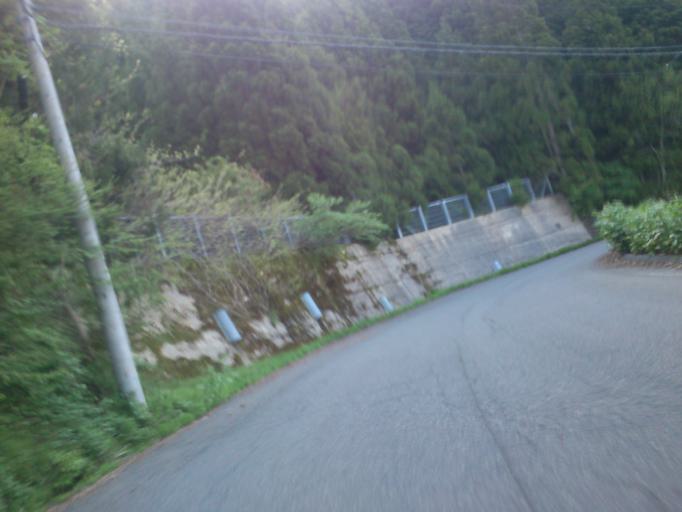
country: JP
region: Kyoto
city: Miyazu
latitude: 35.7158
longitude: 135.1945
